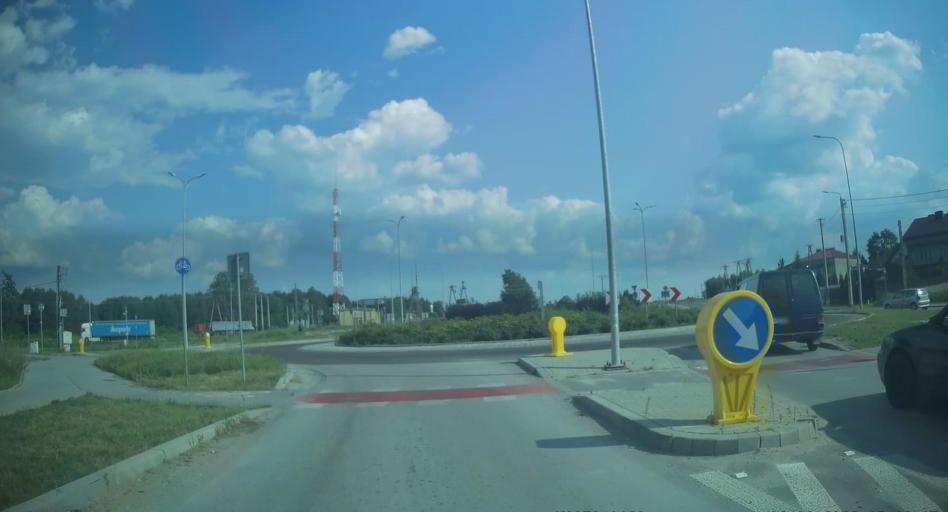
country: PL
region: Swietokrzyskie
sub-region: Powiat konecki
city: Radoszyce
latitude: 51.0714
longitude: 20.2680
